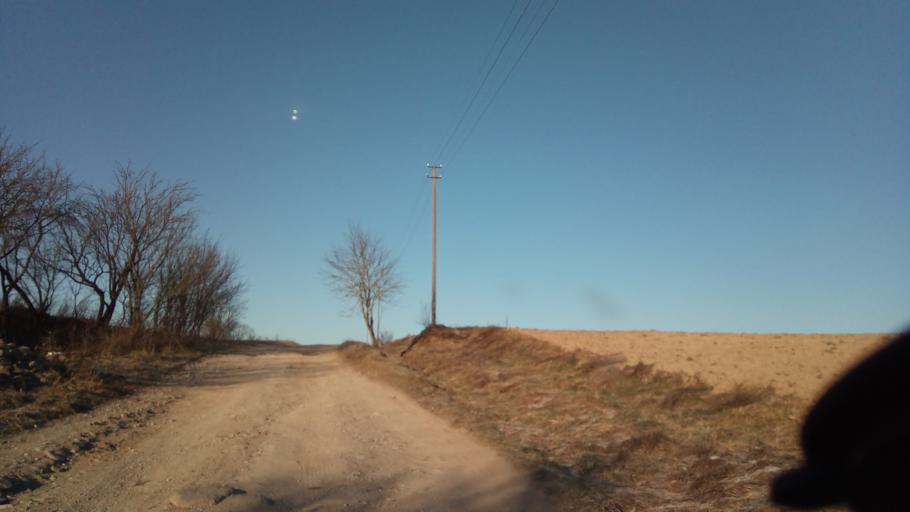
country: LT
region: Alytaus apskritis
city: Druskininkai
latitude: 54.0999
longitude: 24.0119
